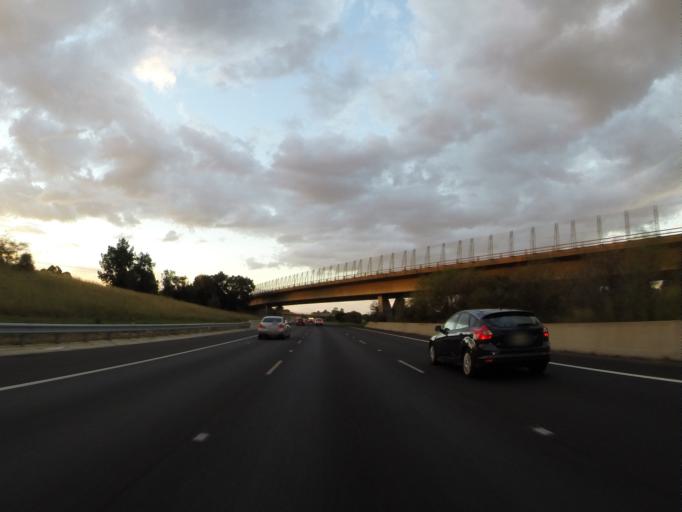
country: AU
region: New South Wales
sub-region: Campbelltown Municipality
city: Leumeah
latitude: -34.0344
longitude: 150.8237
